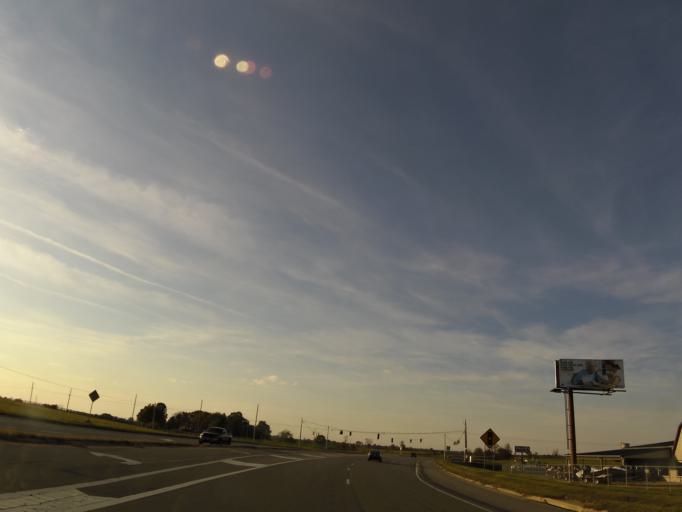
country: US
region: Kentucky
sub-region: Garrard County
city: Lancaster
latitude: 37.6900
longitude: -84.6625
